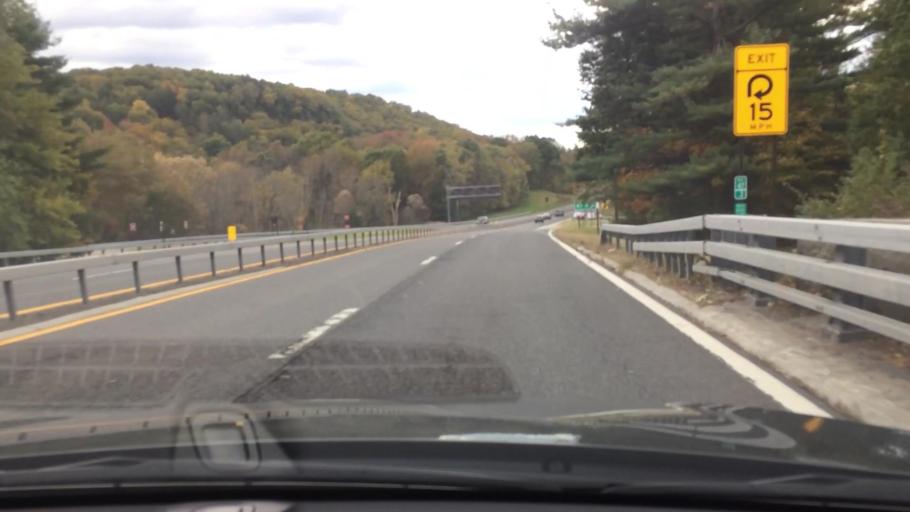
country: US
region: New York
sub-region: Dutchess County
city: Hillside Lake
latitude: 41.6700
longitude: -73.7887
